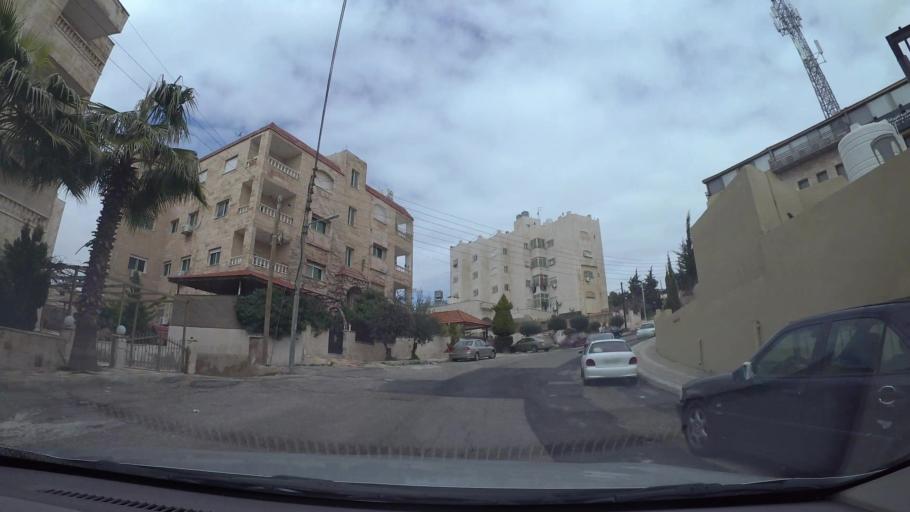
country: JO
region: Amman
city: Al Jubayhah
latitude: 31.9915
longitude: 35.8574
